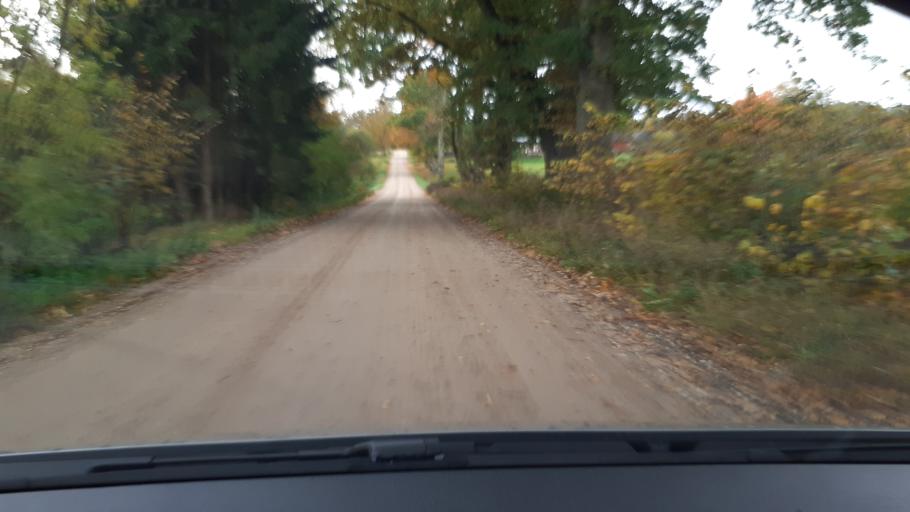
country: LV
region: Kuldigas Rajons
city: Kuldiga
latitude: 57.0287
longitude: 21.9153
